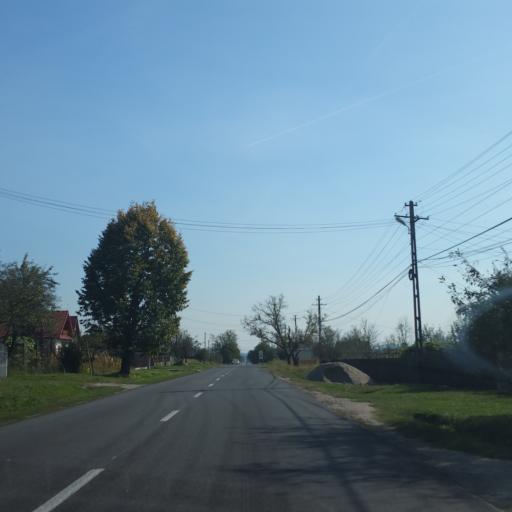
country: RO
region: Arges
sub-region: Comuna Baiculesti
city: Baiculesti
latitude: 45.0800
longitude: 24.6820
